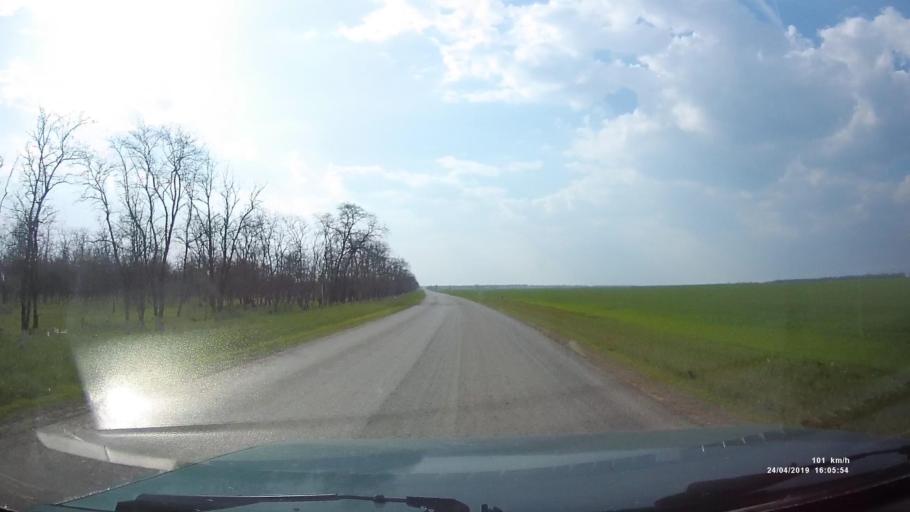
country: RU
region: Rostov
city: Sovetskoye
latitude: 46.6834
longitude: 42.3604
